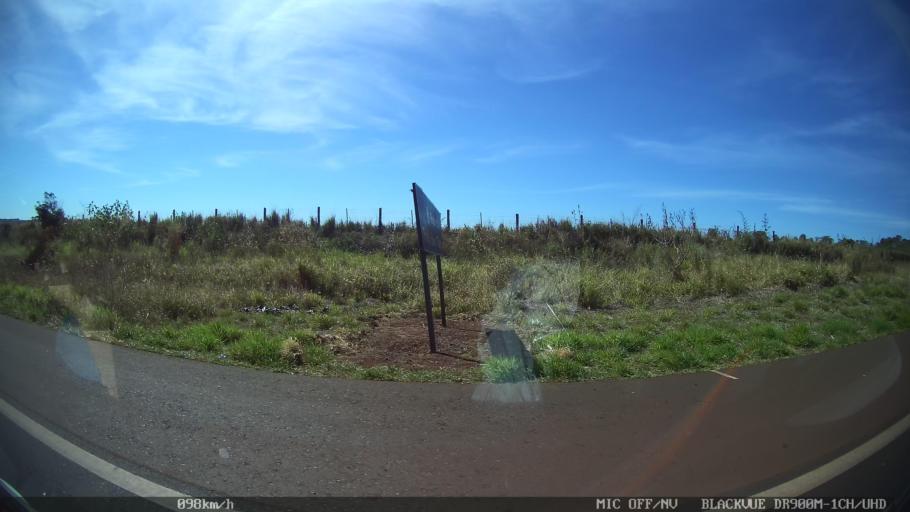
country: BR
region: Sao Paulo
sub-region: Nuporanga
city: Nuporanga
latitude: -20.5579
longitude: -47.6371
